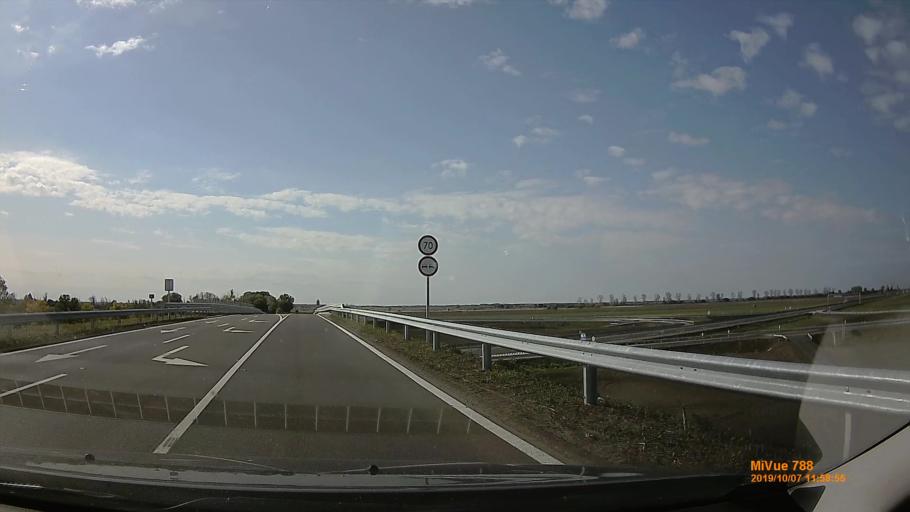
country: HU
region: Bekes
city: Szarvas
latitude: 46.8197
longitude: 20.5178
